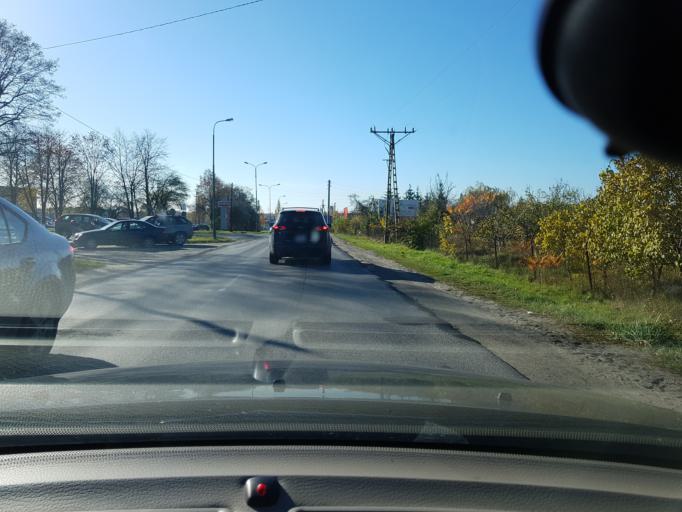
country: PL
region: Lodz Voivodeship
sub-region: Powiat tomaszowski
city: Tomaszow Mazowiecki
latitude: 51.5583
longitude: 20.0197
